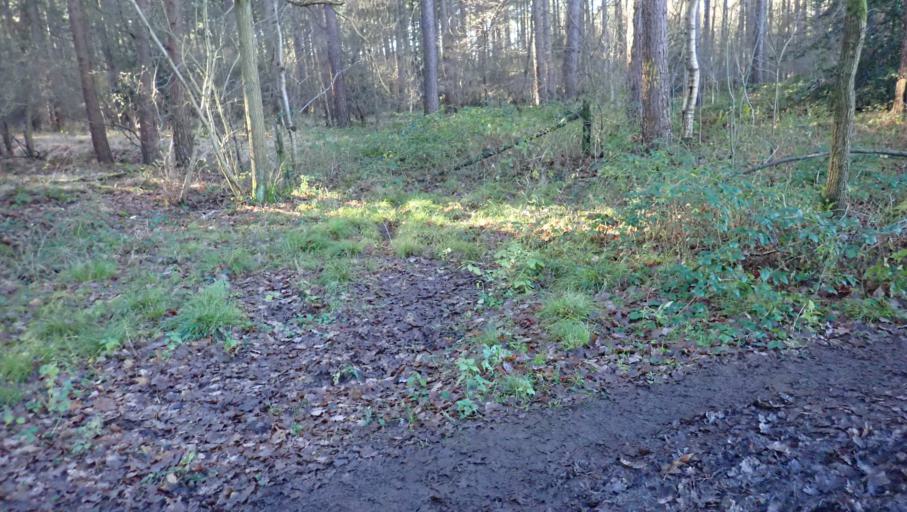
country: BE
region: Flanders
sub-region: Provincie Antwerpen
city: Schilde
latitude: 51.2394
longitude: 4.6238
